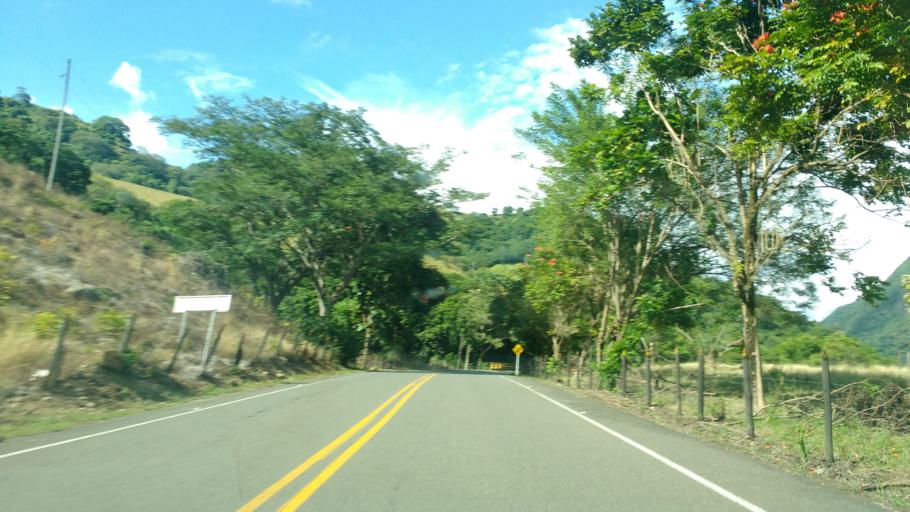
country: CO
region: Antioquia
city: Concordia
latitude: 6.0565
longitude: -75.8668
